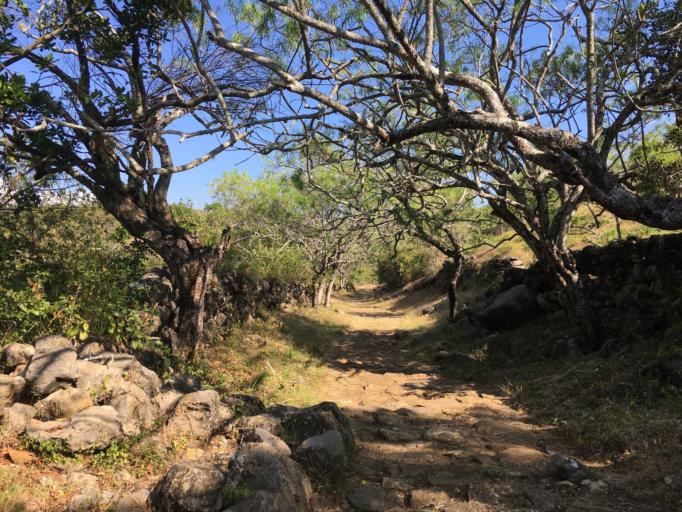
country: CO
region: Santander
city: Barichara
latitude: 6.6572
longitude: -73.2297
